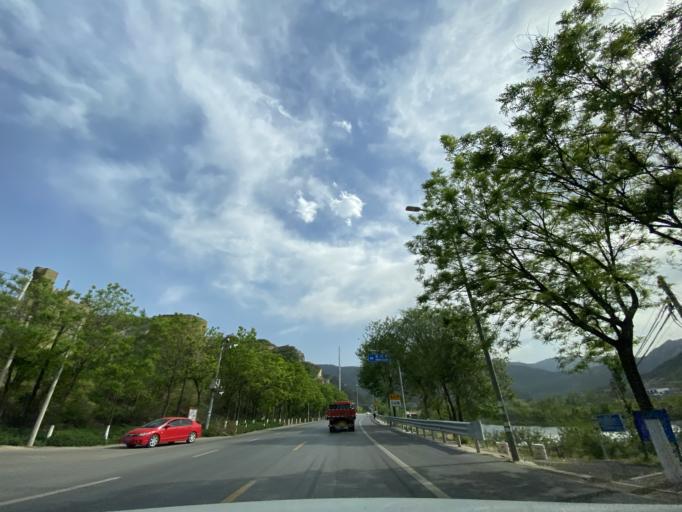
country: CN
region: Beijing
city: Miaofengshan
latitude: 39.9831
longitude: 116.0609
